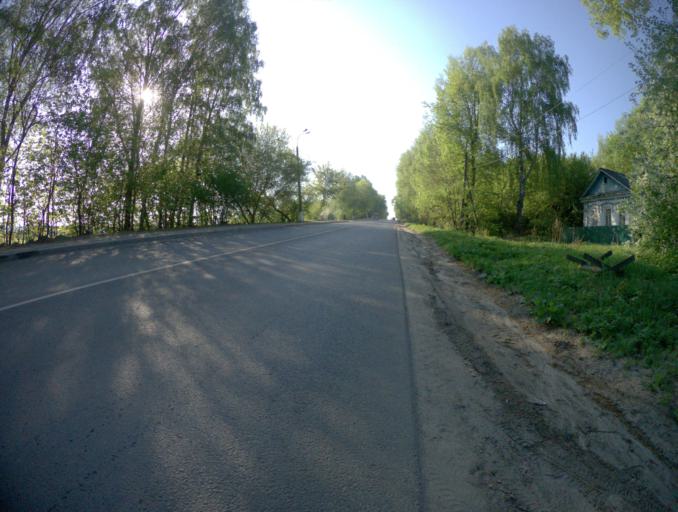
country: RU
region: Vladimir
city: Vyazniki
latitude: 56.2423
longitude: 42.1669
